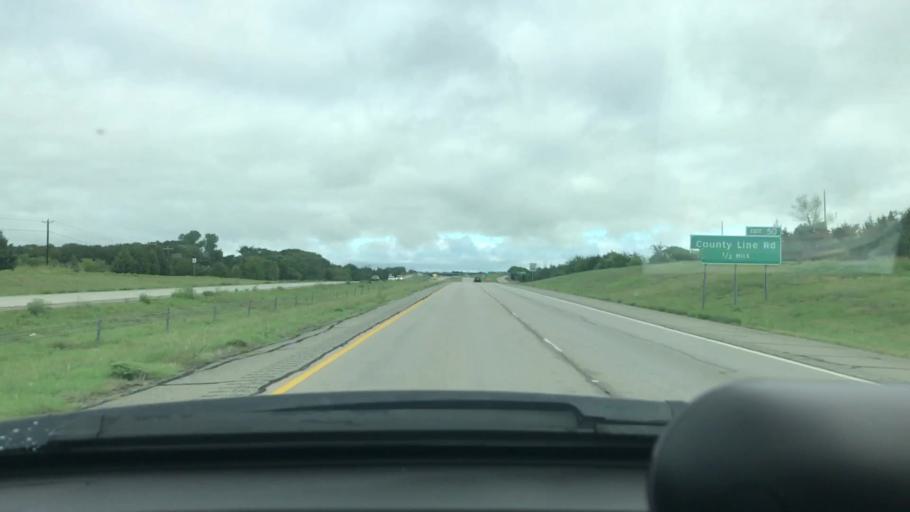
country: US
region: Texas
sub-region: Grayson County
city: Van Alstyne
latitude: 33.3895
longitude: -96.5805
